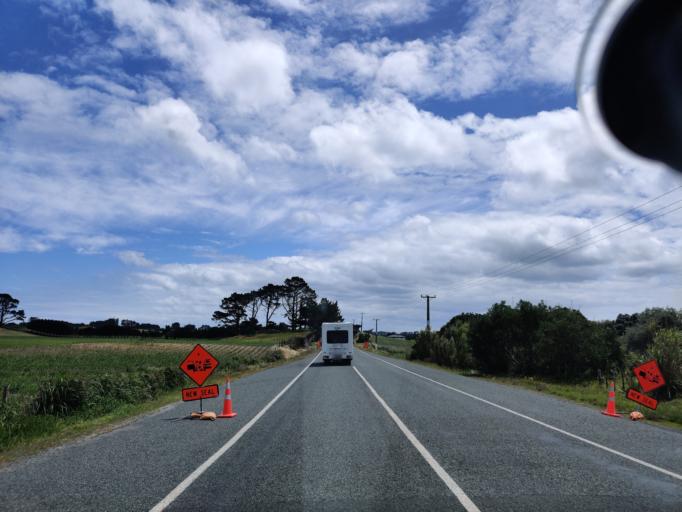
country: NZ
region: Northland
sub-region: Far North District
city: Kaitaia
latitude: -34.7800
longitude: 173.0948
